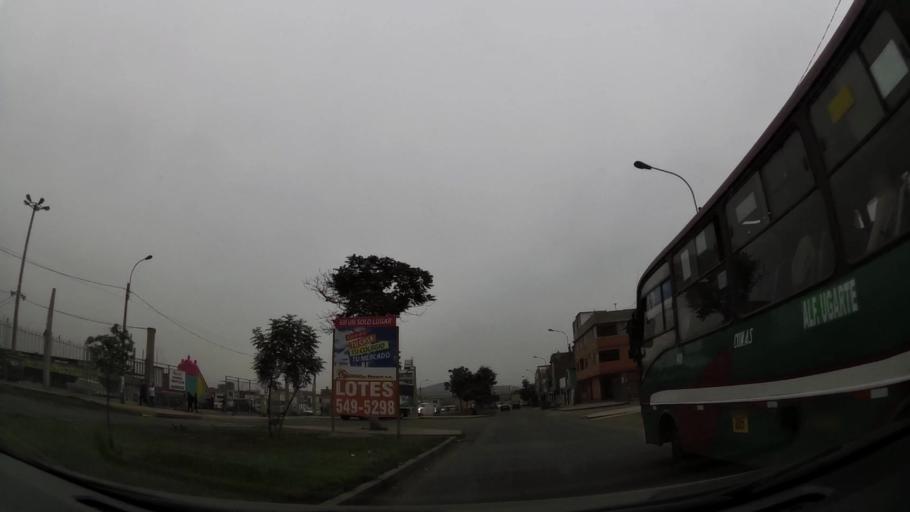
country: PE
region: Lima
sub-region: Lima
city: Independencia
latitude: -11.9376
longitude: -77.0663
